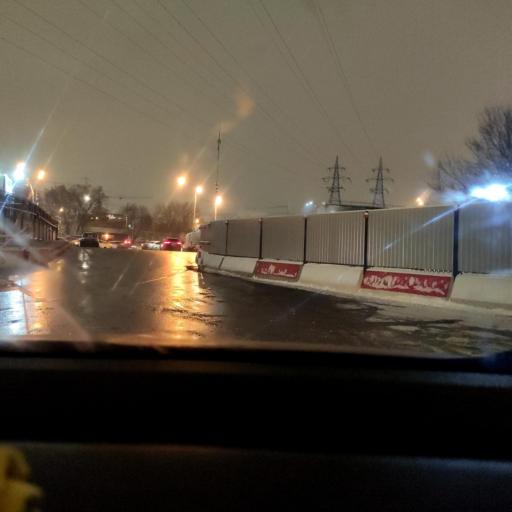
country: RU
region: Moscow
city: Tekstil'shchiki
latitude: 55.7153
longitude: 37.7095
